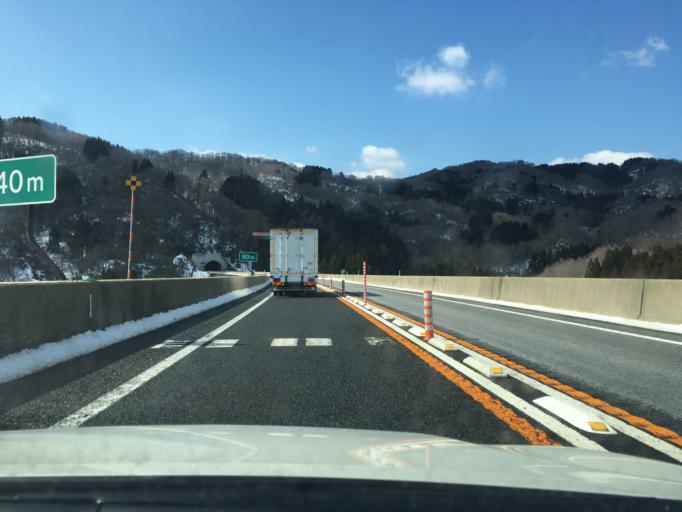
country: JP
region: Yamagata
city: Tsuruoka
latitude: 38.5921
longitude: 139.8853
